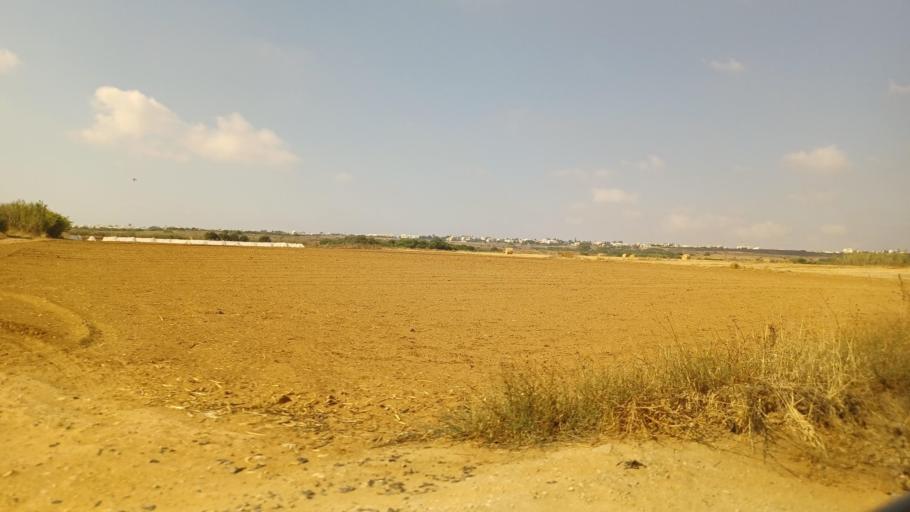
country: CY
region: Ammochostos
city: Paralimni
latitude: 35.0692
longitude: 33.9938
